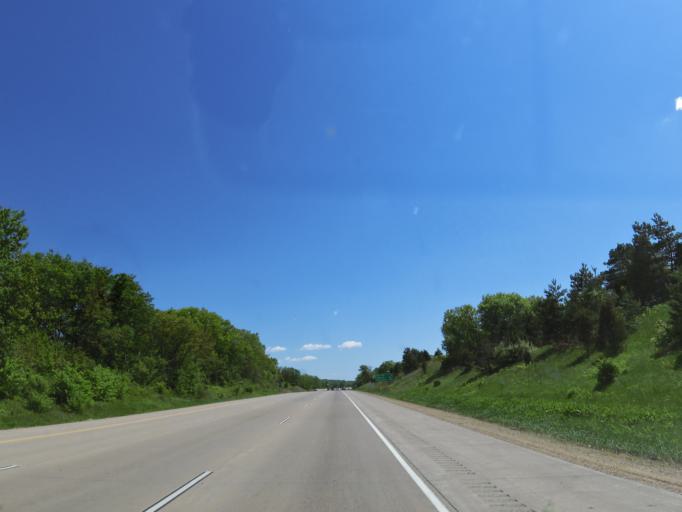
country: US
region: Wisconsin
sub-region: Columbia County
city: Poynette
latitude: 43.3817
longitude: -89.4637
